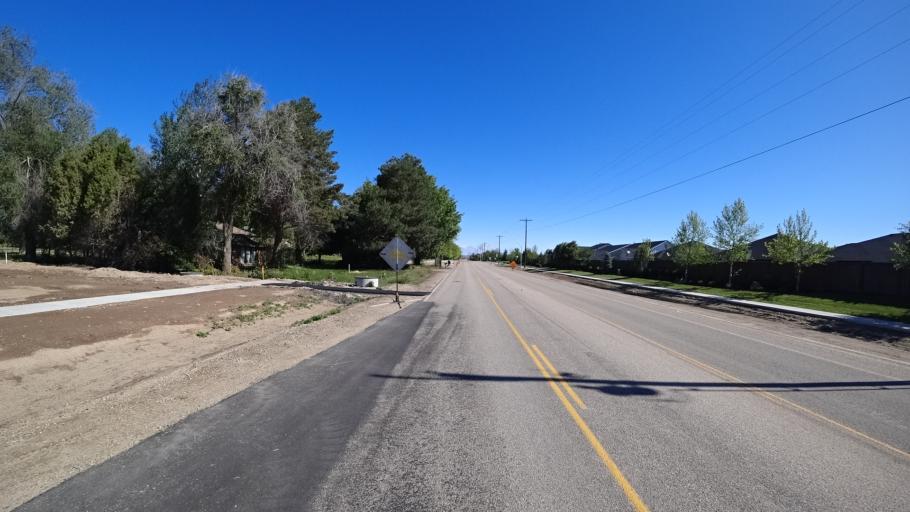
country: US
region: Idaho
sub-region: Ada County
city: Star
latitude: 43.6563
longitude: -116.4536
